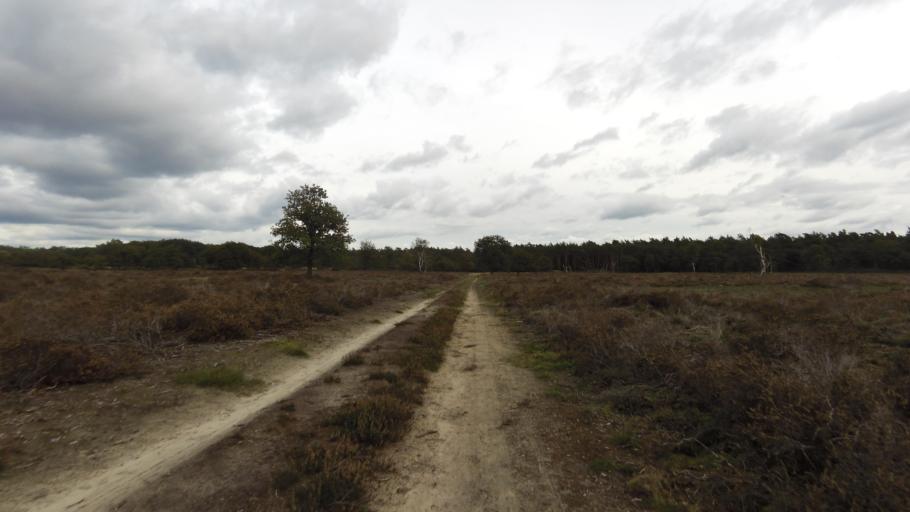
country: NL
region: Gelderland
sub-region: Gemeente Barneveld
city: Stroe
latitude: 52.1813
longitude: 5.7239
